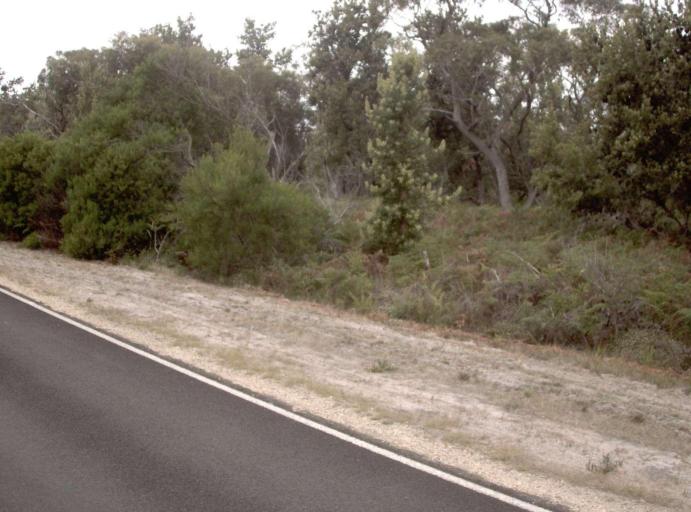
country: AU
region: Victoria
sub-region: East Gippsland
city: Bairnsdale
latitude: -38.0731
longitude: 147.5449
